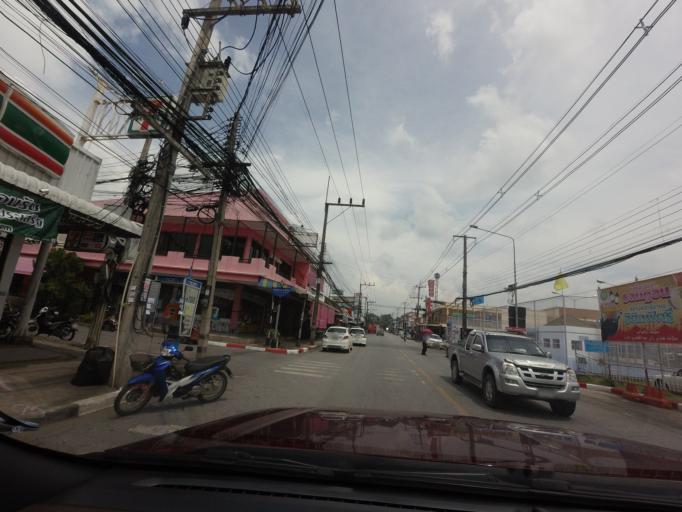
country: TH
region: Yala
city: Yala
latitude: 6.5309
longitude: 101.2846
